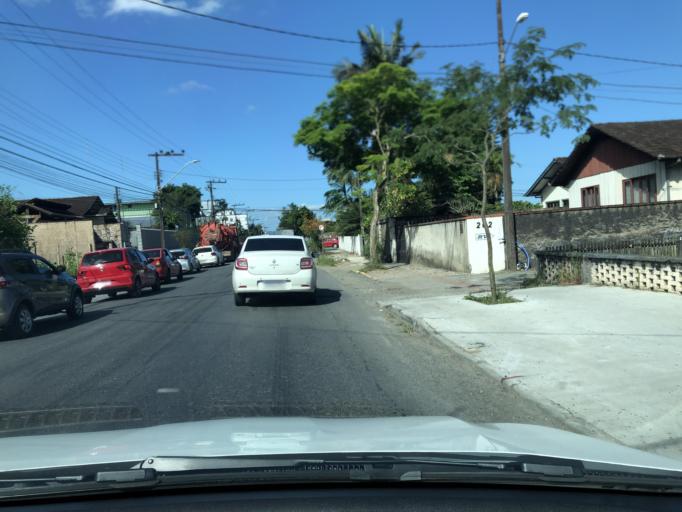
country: BR
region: Santa Catarina
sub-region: Joinville
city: Joinville
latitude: -26.3105
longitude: -48.8303
